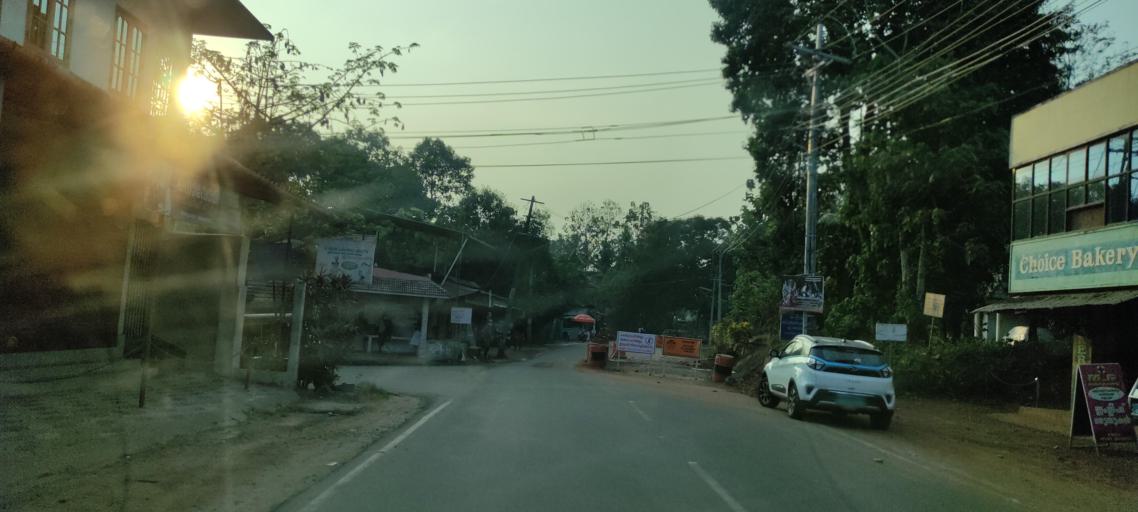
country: IN
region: Kerala
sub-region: Alappuzha
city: Mavelikara
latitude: 9.2496
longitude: 76.5780
